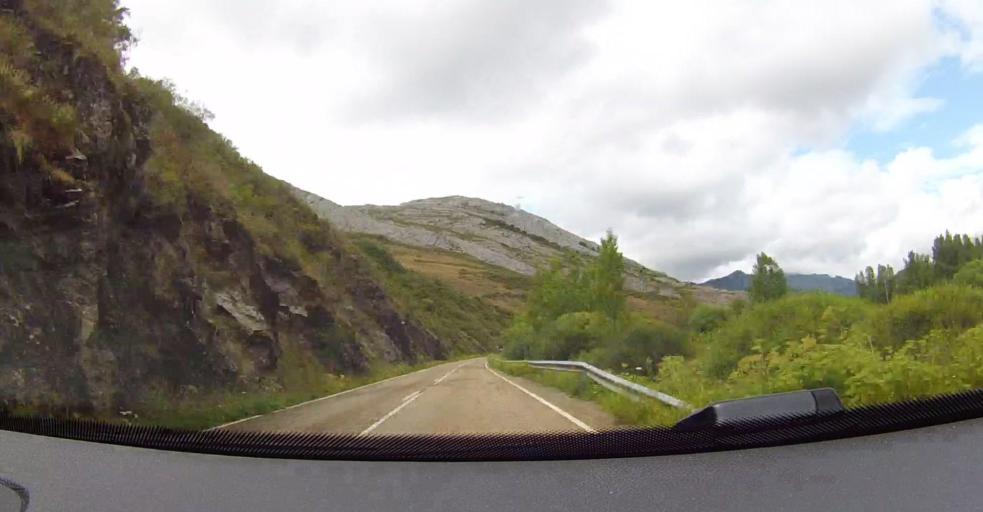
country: ES
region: Castille and Leon
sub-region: Provincia de Leon
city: Puebla de Lillo
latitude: 42.9894
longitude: -5.2601
